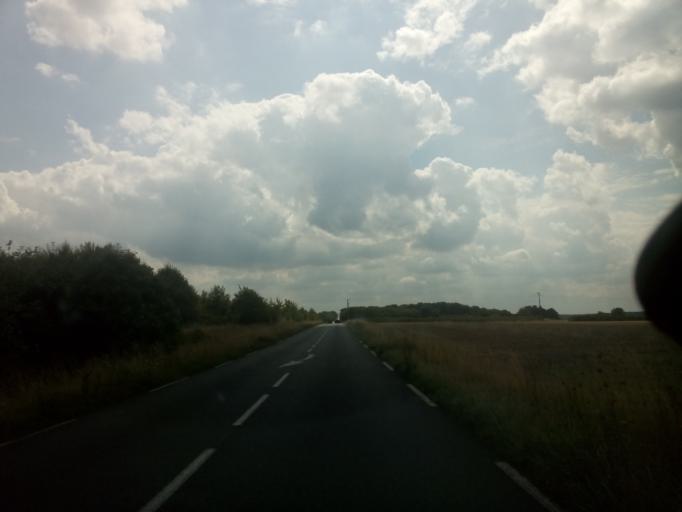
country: FR
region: Centre
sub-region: Departement d'Indre-et-Loire
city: Cheille
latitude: 47.2865
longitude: 0.4227
